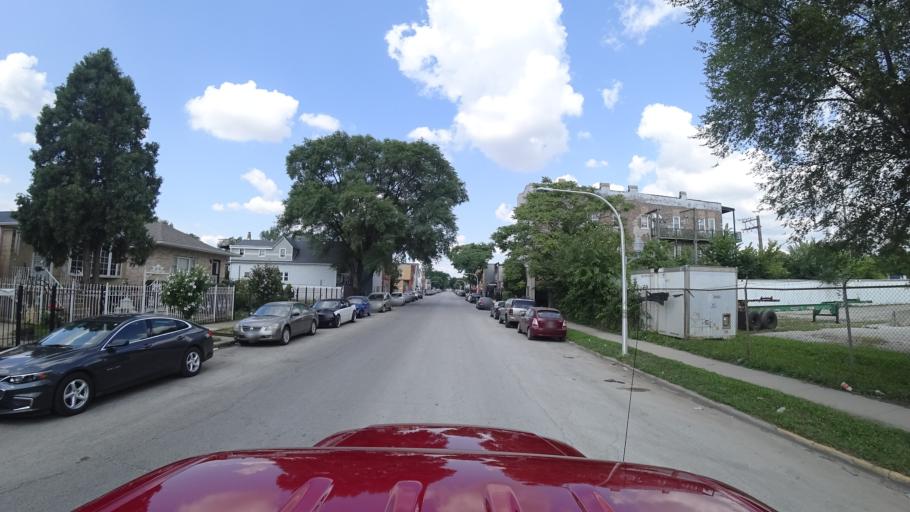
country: US
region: Illinois
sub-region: Cook County
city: Chicago
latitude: 41.8246
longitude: -87.6958
